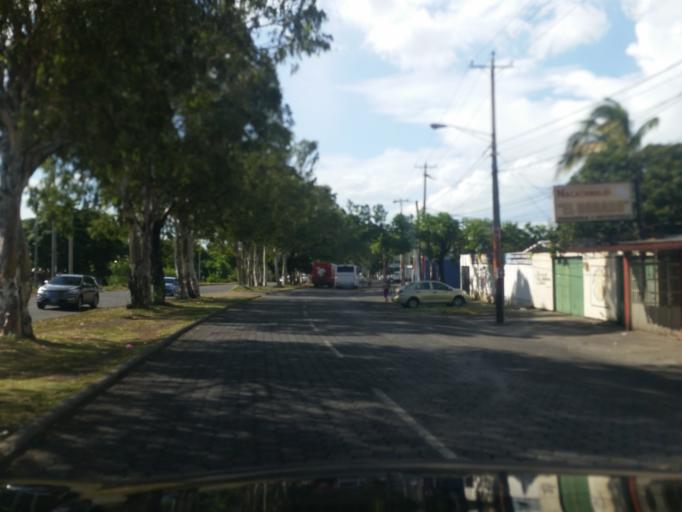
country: NI
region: Managua
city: Managua
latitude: 12.1314
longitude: -86.2478
